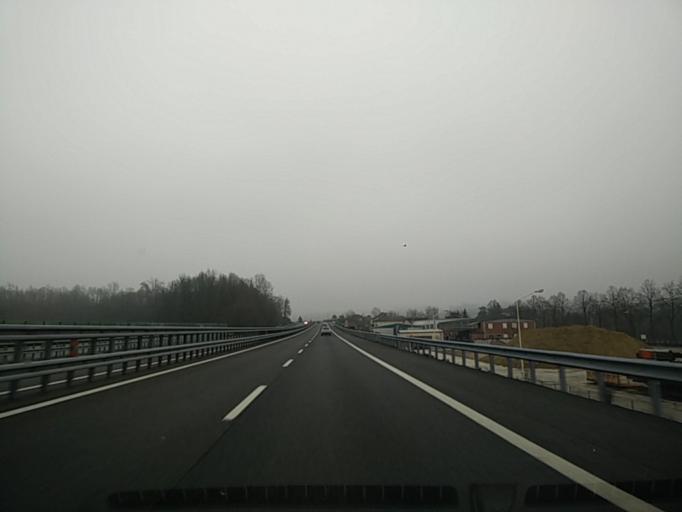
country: IT
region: Piedmont
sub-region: Provincia di Asti
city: Cantarana
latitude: 44.9063
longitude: 8.0538
